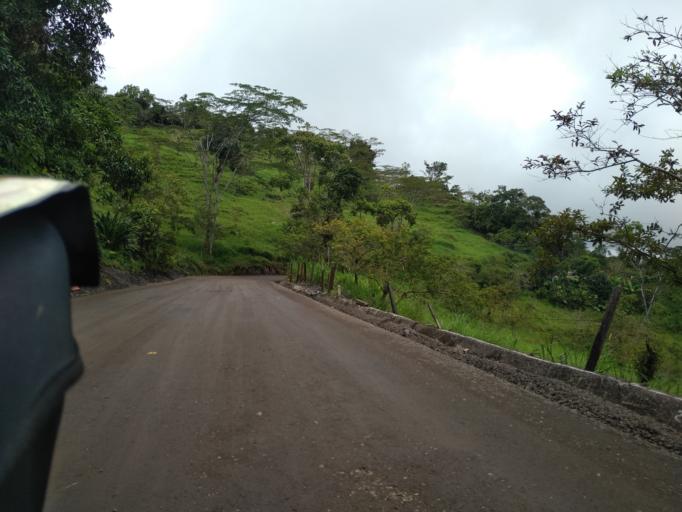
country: CO
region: Santander
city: Landazuri
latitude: 6.1771
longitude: -73.7136
